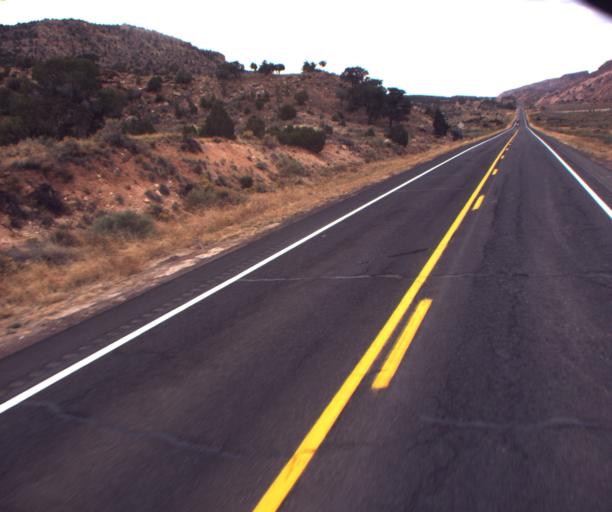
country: US
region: Arizona
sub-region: Navajo County
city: Kayenta
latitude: 36.6741
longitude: -110.3979
